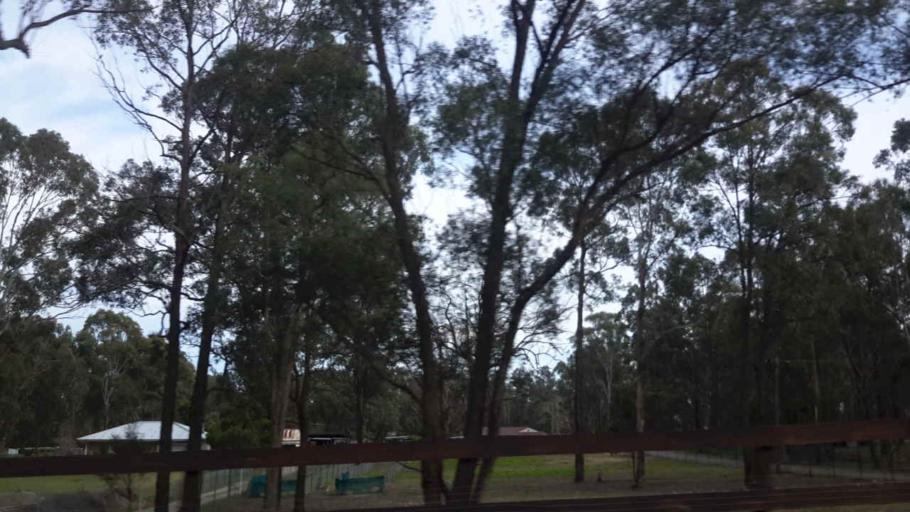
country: AU
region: New South Wales
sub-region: Hawkesbury
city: South Windsor
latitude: -33.6441
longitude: 150.7832
